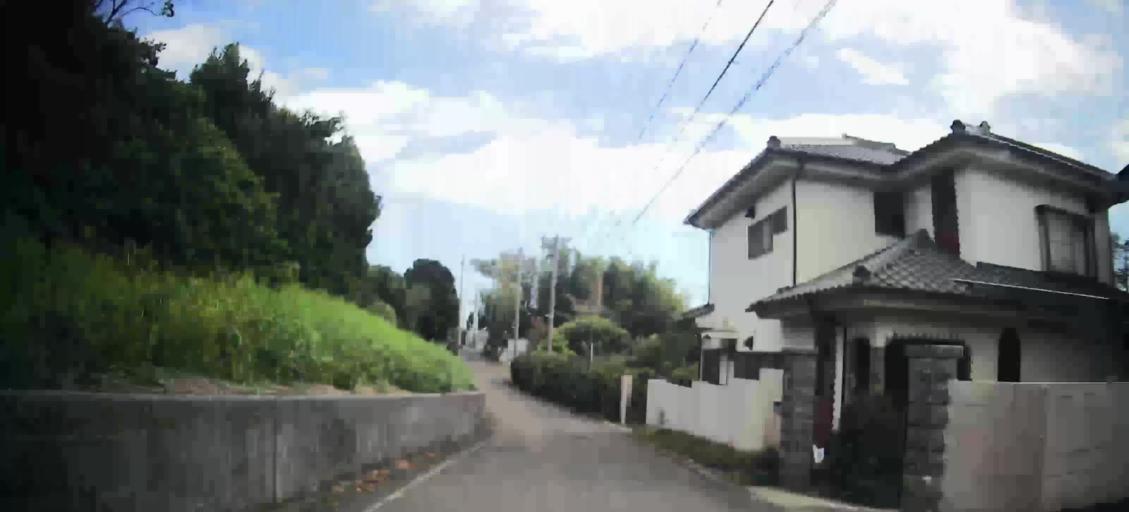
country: JP
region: Kanagawa
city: Yokohama
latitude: 35.4851
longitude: 139.5774
